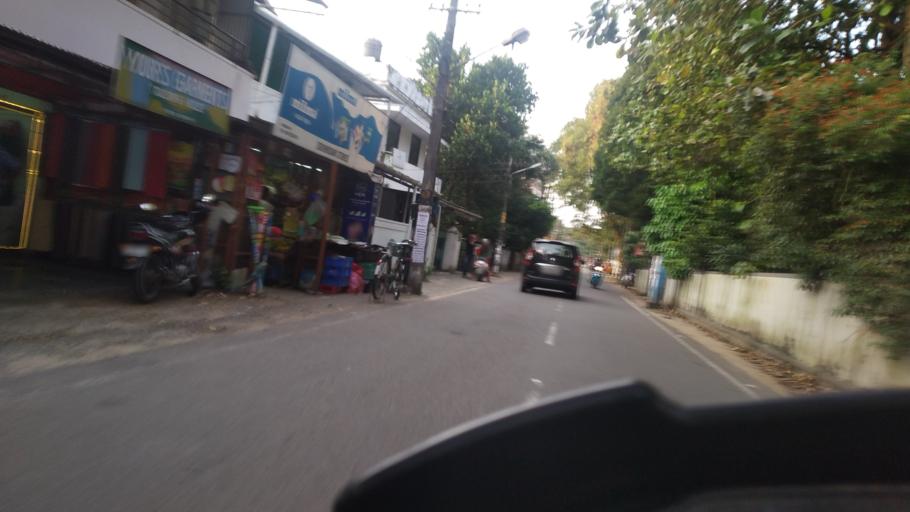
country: IN
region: Kerala
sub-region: Ernakulam
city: Elur
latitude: 10.0287
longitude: 76.2980
